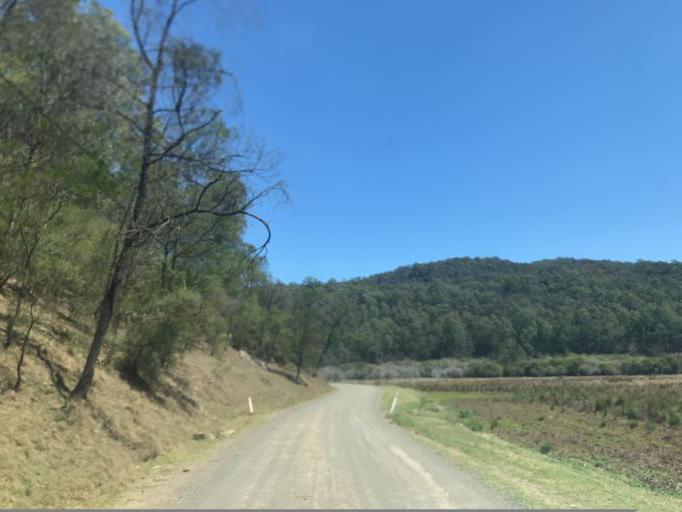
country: AU
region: New South Wales
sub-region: Hornsby Shire
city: Glenorie
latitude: -33.2467
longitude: 150.9773
